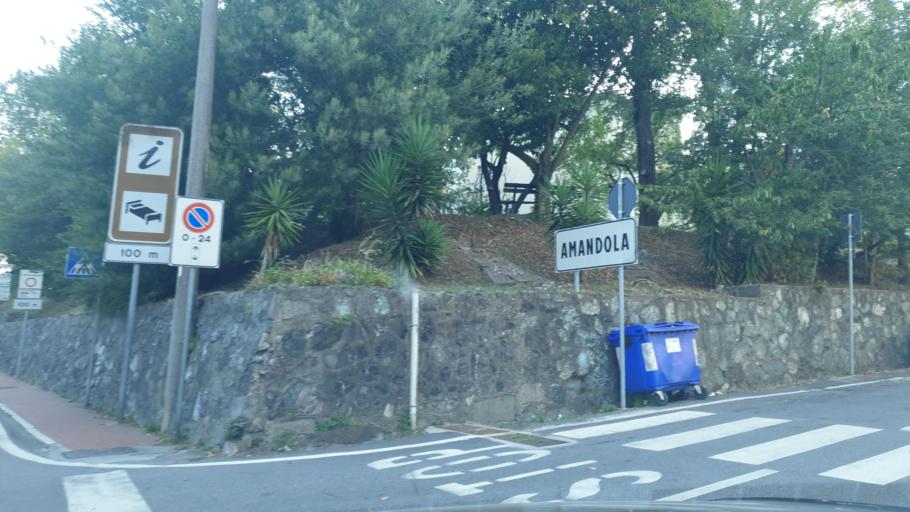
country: IT
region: Liguria
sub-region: Provincia di La Spezia
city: Levanto
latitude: 44.1769
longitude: 9.6204
